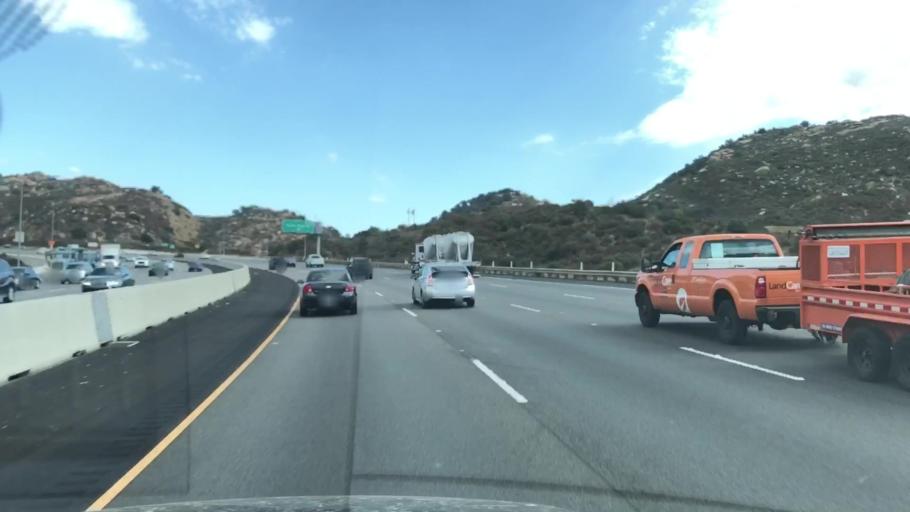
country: US
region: California
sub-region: Los Angeles County
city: Chatsworth
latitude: 34.2667
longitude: -118.6421
